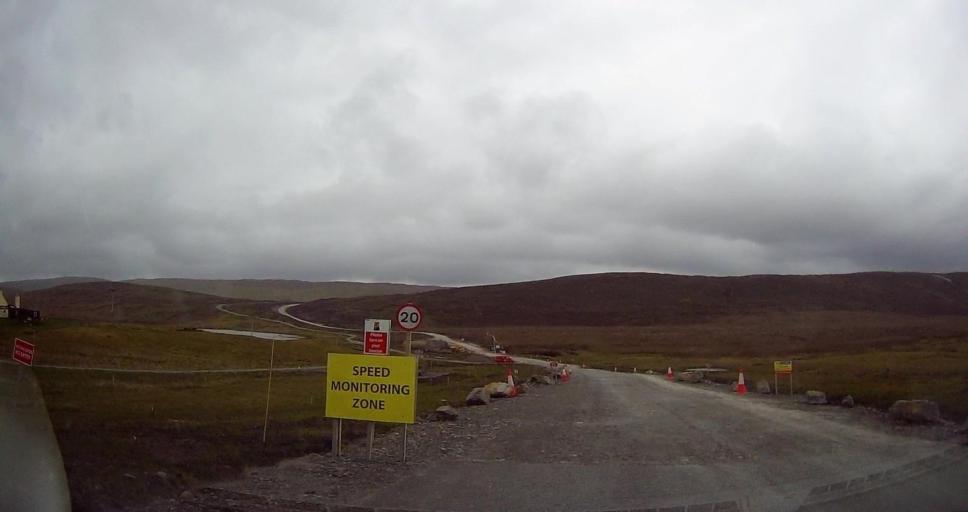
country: GB
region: Scotland
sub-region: Shetland Islands
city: Lerwick
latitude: 60.2795
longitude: -1.2451
